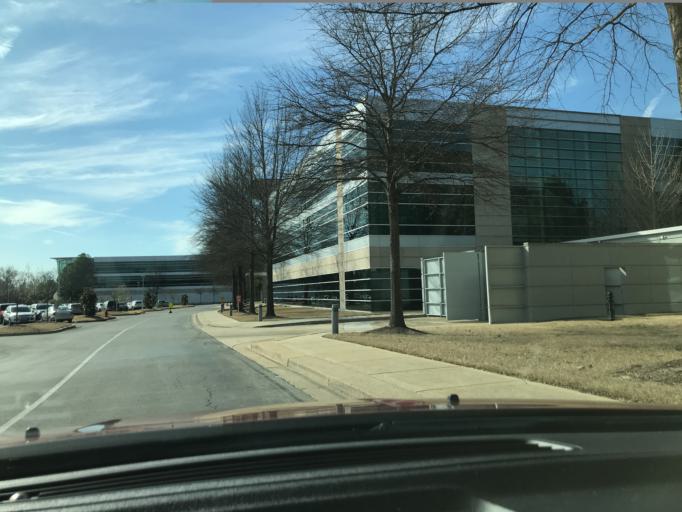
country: US
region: Tennessee
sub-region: Shelby County
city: Germantown
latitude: 35.0507
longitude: -89.7905
